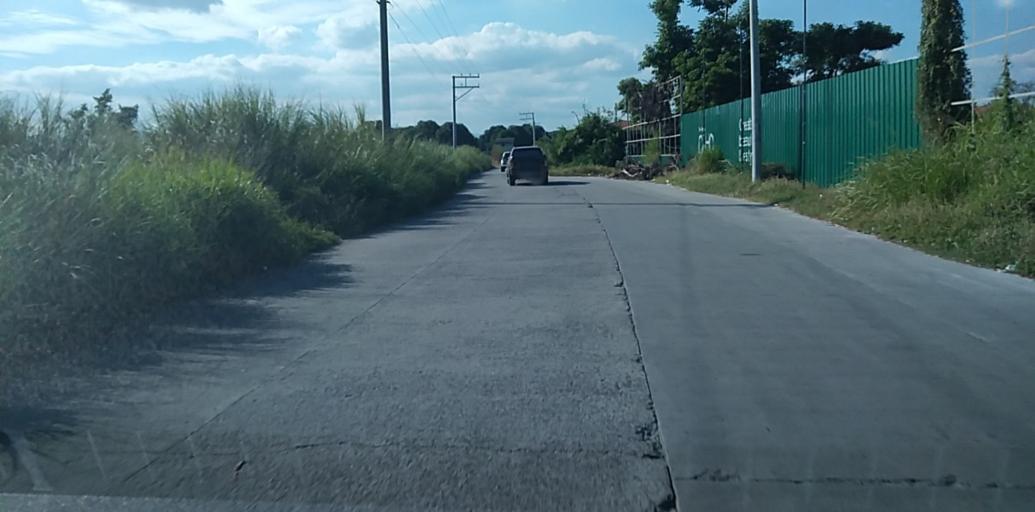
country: PH
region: Central Luzon
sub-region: Province of Pampanga
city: Acli
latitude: 15.1099
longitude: 120.6524
